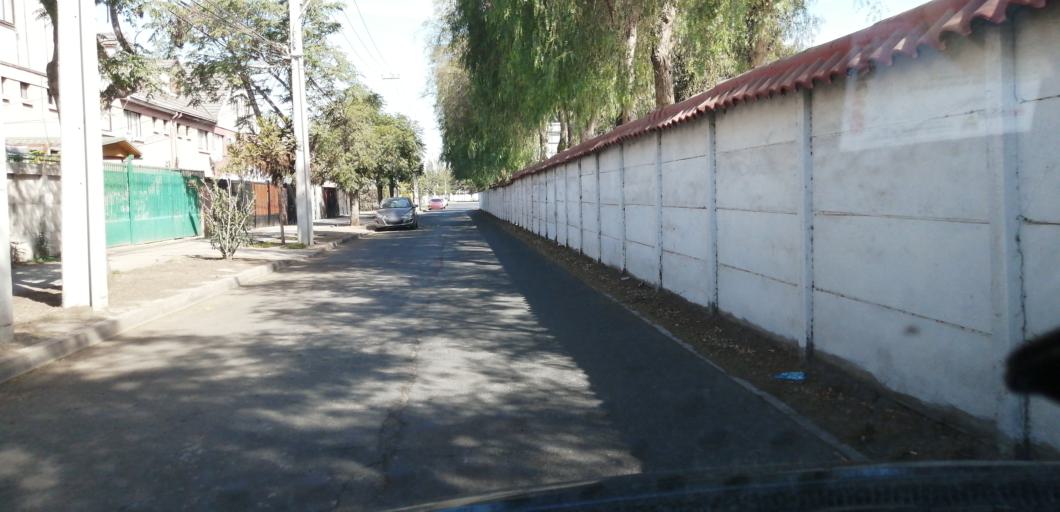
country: CL
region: Santiago Metropolitan
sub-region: Provincia de Santiago
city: Lo Prado
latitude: -33.4624
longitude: -70.7252
